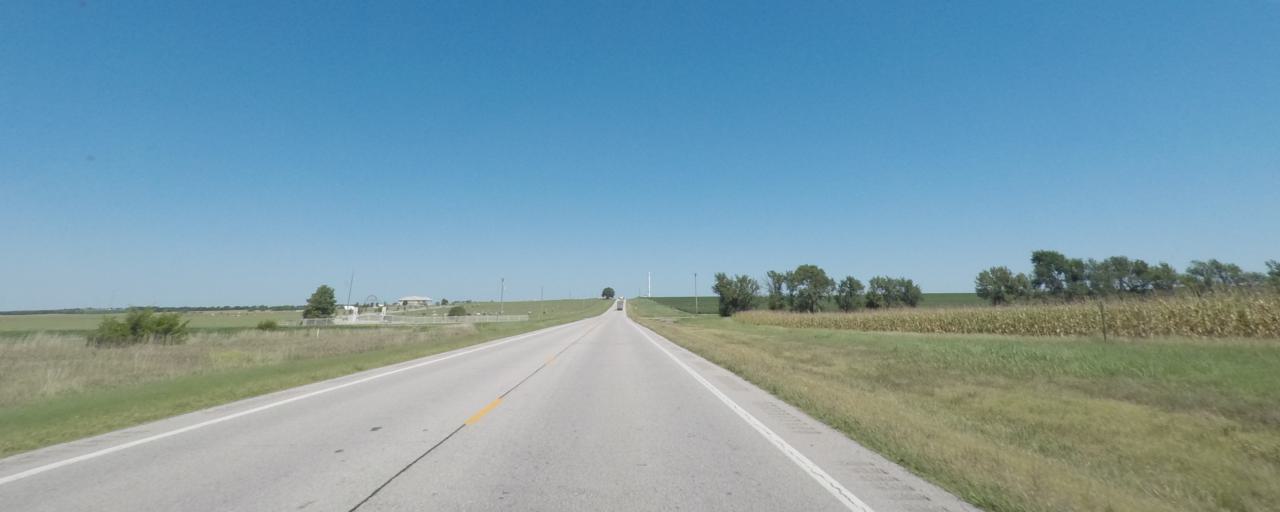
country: US
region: Kansas
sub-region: Sumner County
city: Wellington
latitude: 37.3461
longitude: -97.3851
